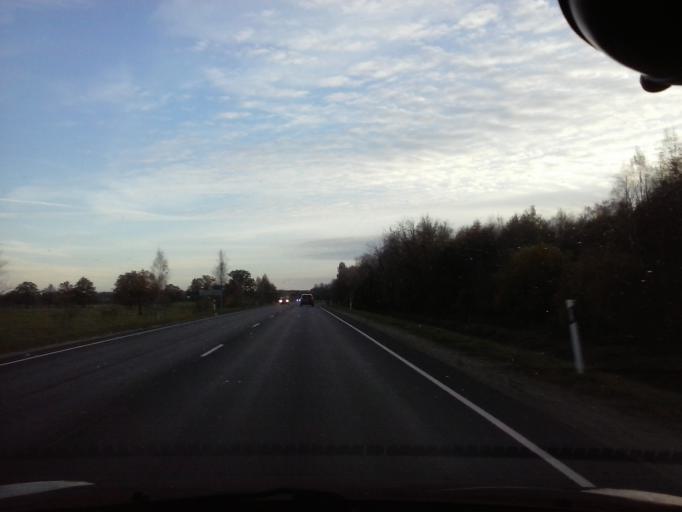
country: EE
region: Harju
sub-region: Nissi vald
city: Turba
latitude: 58.9130
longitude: 24.1116
